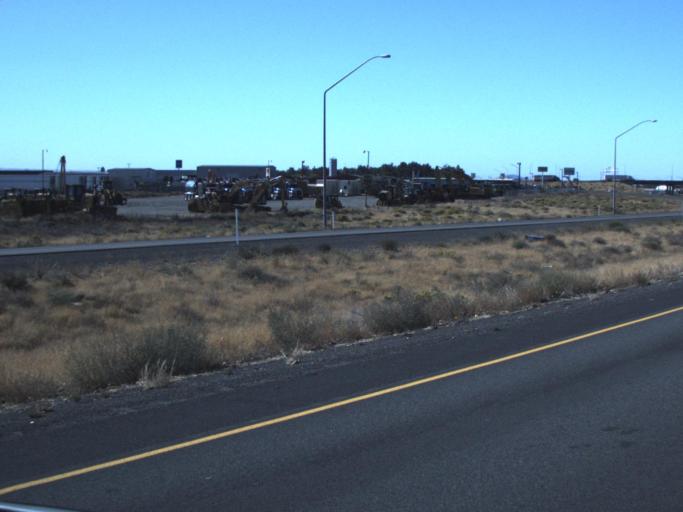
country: US
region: Washington
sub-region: Franklin County
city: Pasco
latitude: 46.2505
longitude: -119.0736
